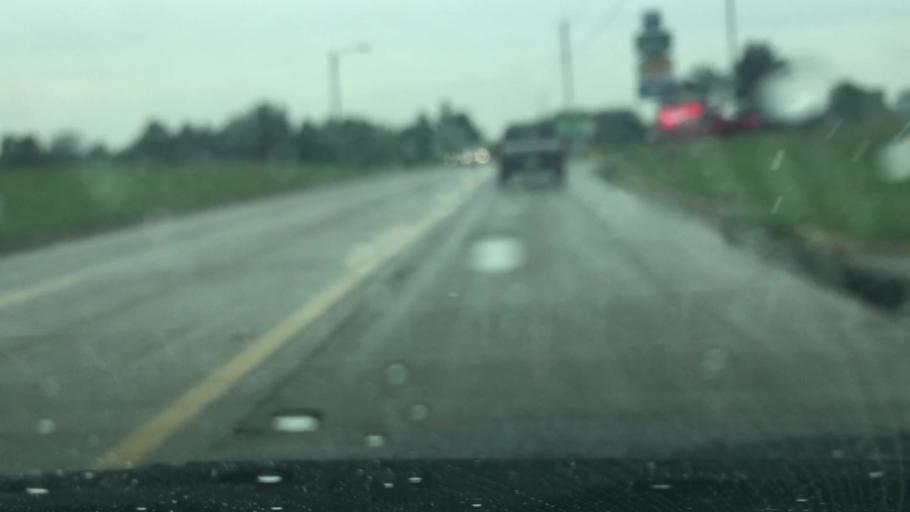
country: US
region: Illinois
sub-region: Williamson County
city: Marion
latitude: 37.7313
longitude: -88.9653
